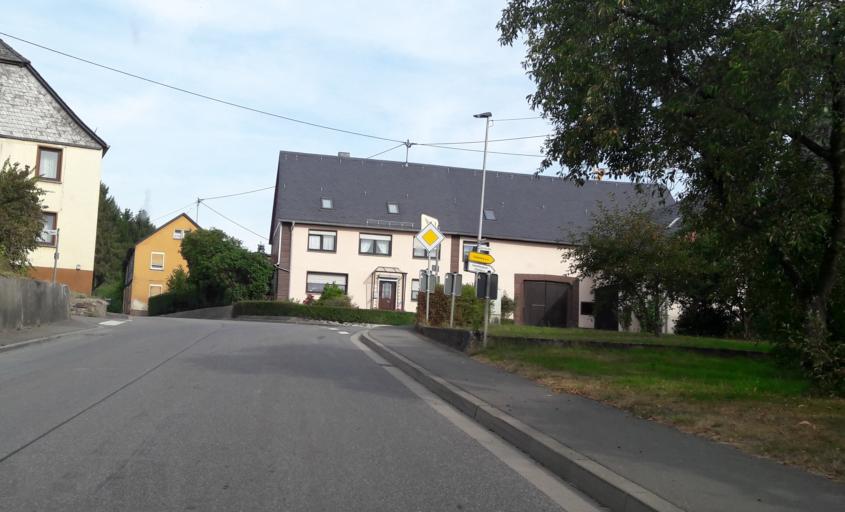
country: DE
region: Rheinland-Pfalz
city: Ellenberg
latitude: 49.6589
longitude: 7.1479
